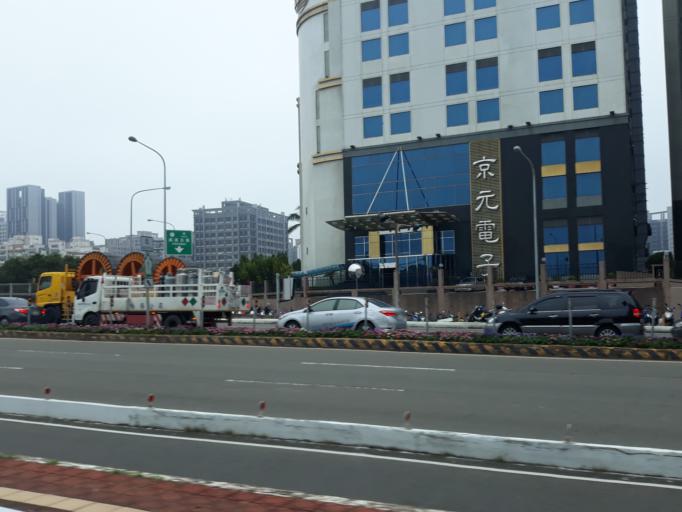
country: TW
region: Taiwan
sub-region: Hsinchu
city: Hsinchu
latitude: 24.7984
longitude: 121.0076
